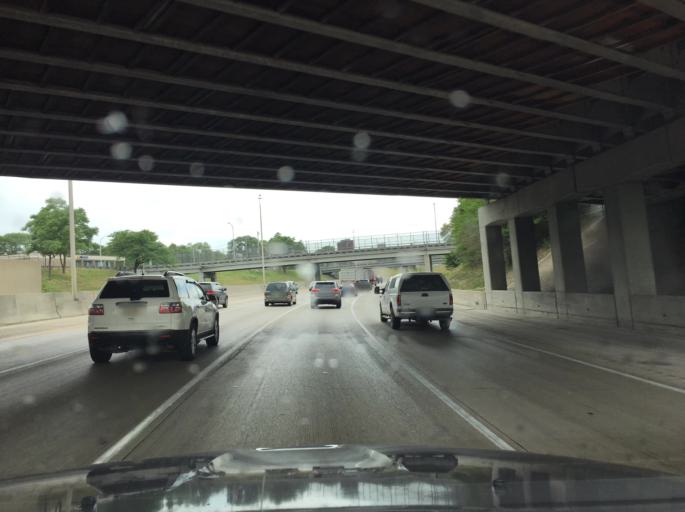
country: US
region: Michigan
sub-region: Oakland County
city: Hazel Park
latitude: 42.4593
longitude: -83.1036
